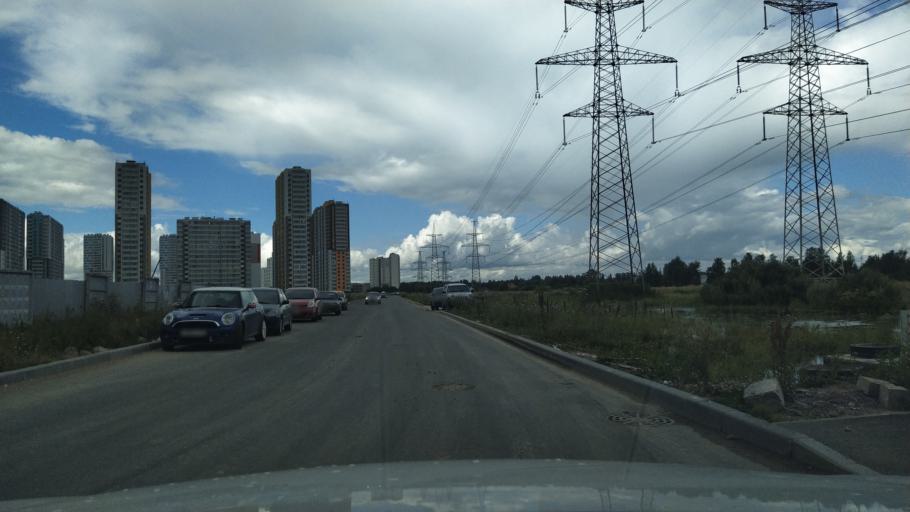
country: RU
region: St.-Petersburg
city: Krasnogvargeisky
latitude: 60.0037
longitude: 30.4832
